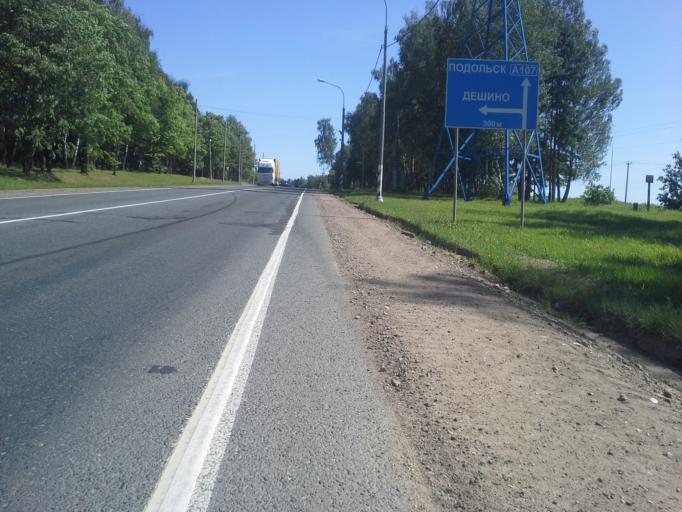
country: RU
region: Moskovskaya
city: Troitsk
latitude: 55.4114
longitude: 37.1975
